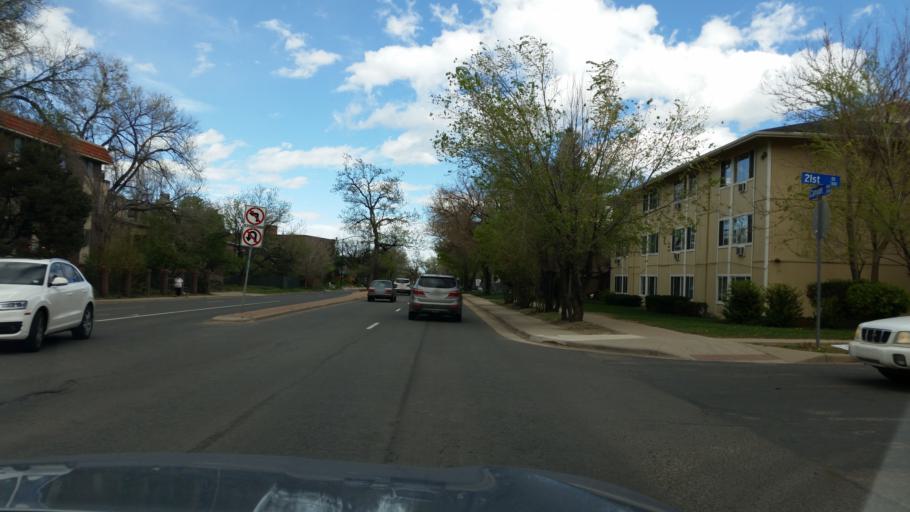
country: US
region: Colorado
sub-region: Boulder County
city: Boulder
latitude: 40.0172
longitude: -105.2681
